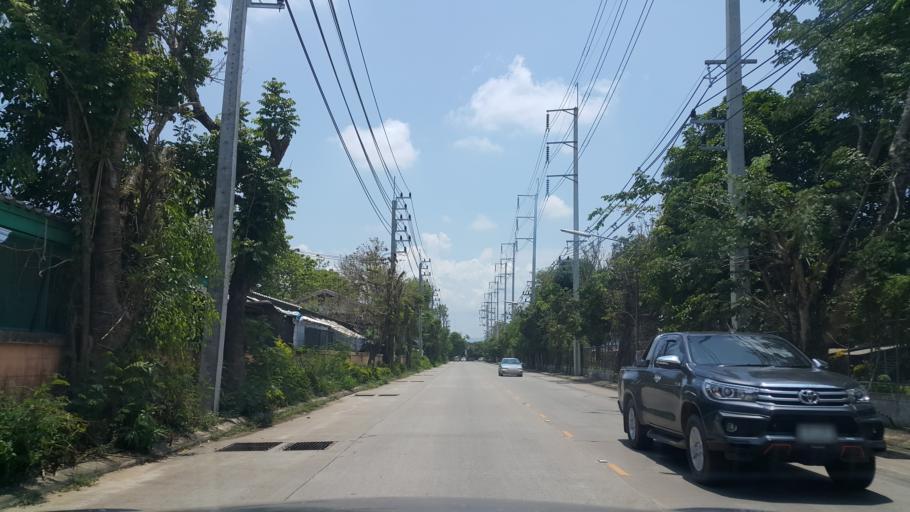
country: TH
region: Chiang Rai
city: Chiang Rai
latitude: 19.9109
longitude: 99.8219
